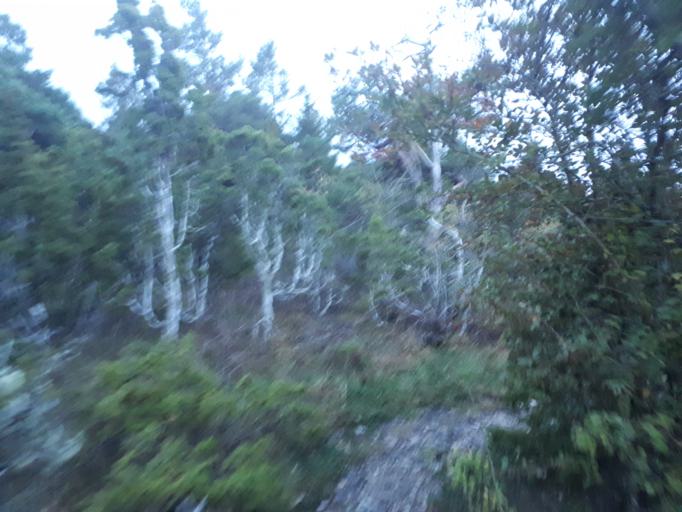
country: SE
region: Gotland
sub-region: Gotland
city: Visby
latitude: 57.6838
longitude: 18.3472
